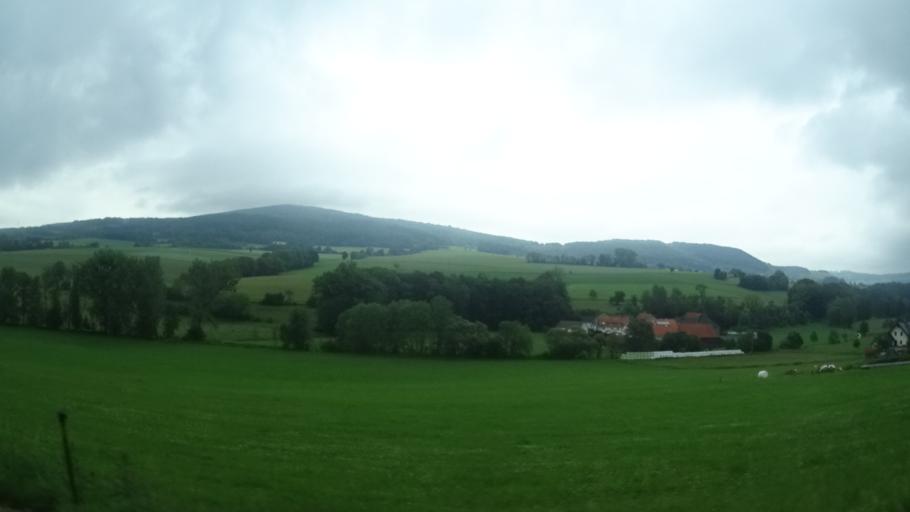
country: DE
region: Hesse
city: Tann
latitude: 50.6232
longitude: 10.0239
